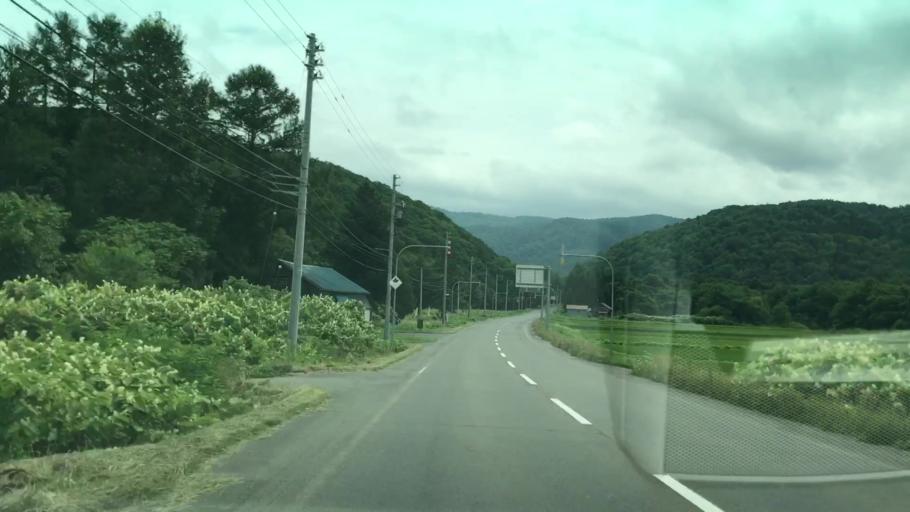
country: JP
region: Hokkaido
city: Yoichi
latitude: 43.0491
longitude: 140.8459
